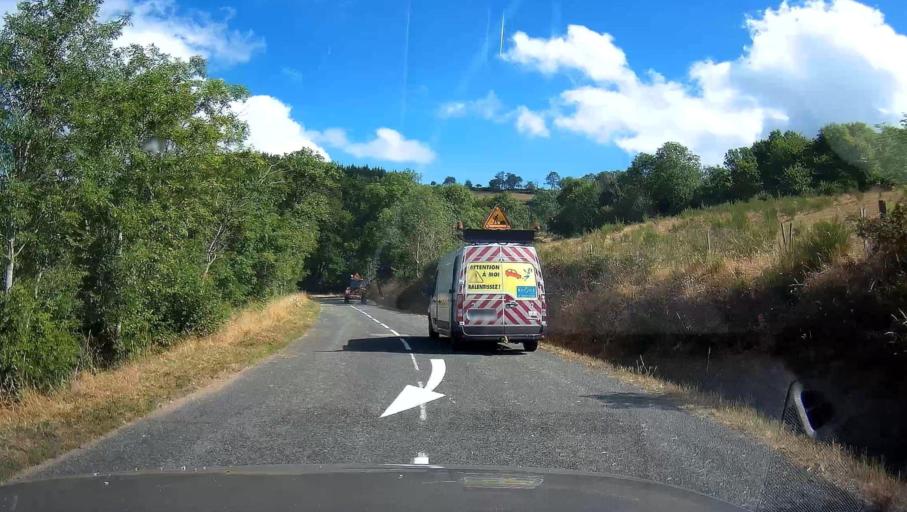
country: FR
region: Rhone-Alpes
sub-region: Departement du Rhone
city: Cogny
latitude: 45.9925
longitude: 4.5596
